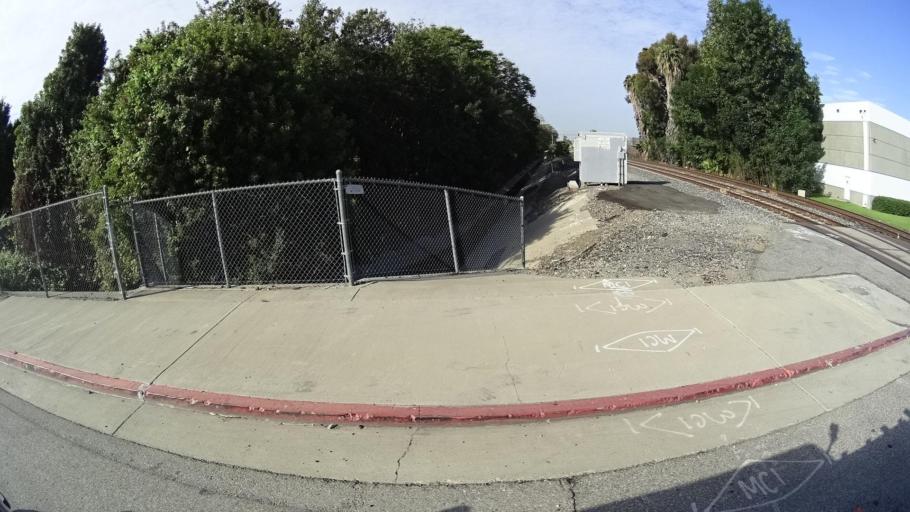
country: US
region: California
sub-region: Los Angeles County
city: South El Monte
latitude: 34.0172
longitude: -118.0469
